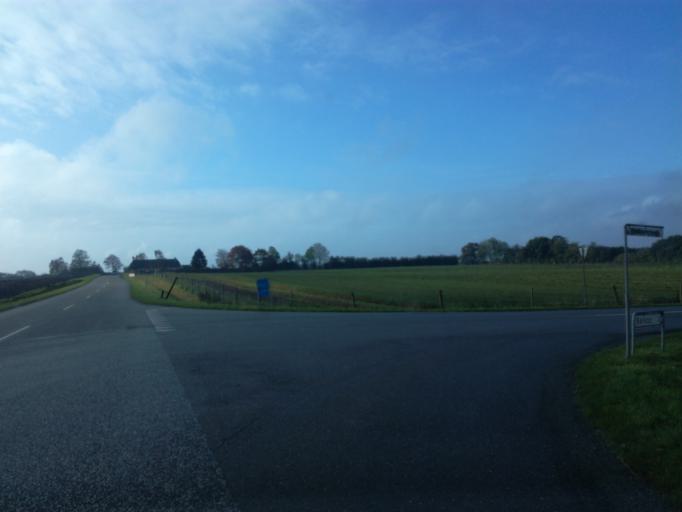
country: DK
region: South Denmark
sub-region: Vejle Kommune
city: Brejning
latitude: 55.6316
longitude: 9.6852
